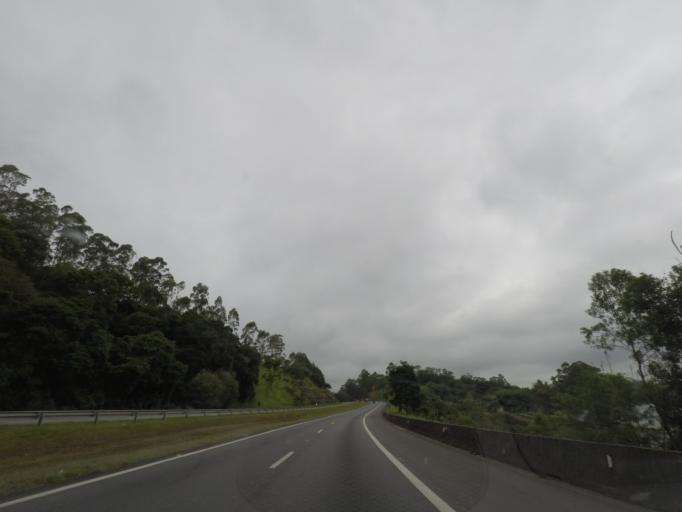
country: BR
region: Sao Paulo
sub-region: Bom Jesus Dos Perdoes
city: Bom Jesus dos Perdoes
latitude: -23.1735
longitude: -46.3852
